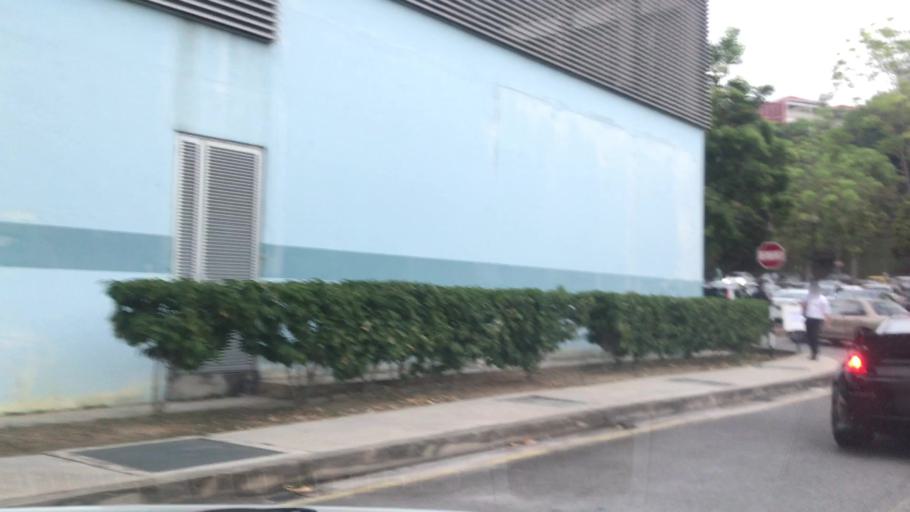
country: MY
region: Kuala Lumpur
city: Kuala Lumpur
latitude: 3.1150
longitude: 101.6580
